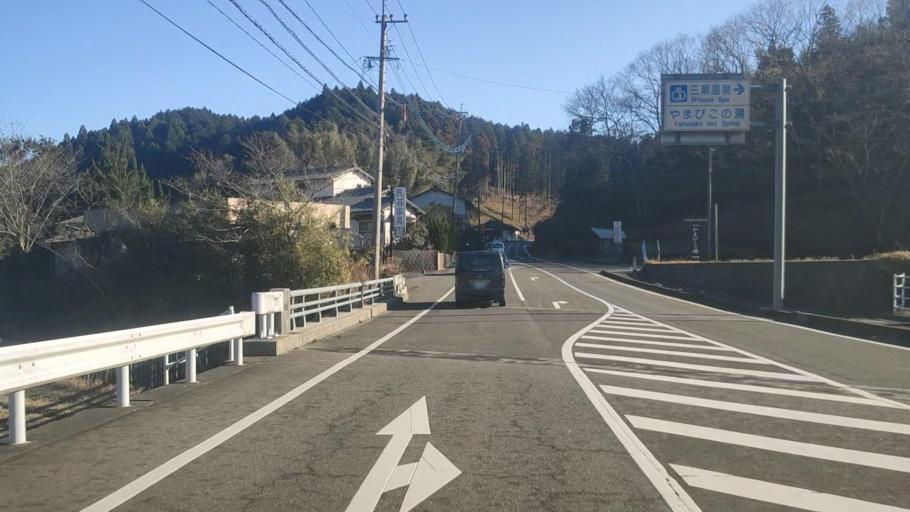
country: JP
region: Saga Prefecture
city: Kanzakimachi-kanzaki
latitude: 33.4217
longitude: 130.2779
